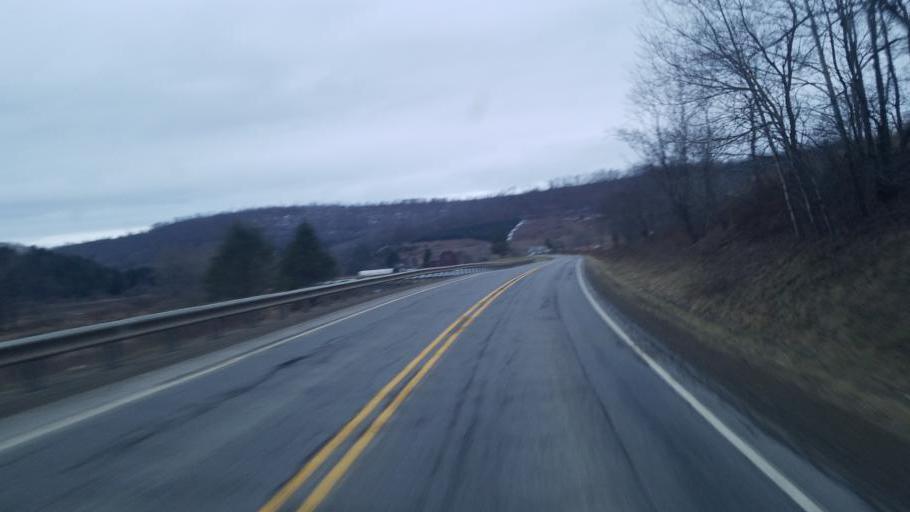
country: US
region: Pennsylvania
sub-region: Potter County
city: Coudersport
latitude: 41.8348
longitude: -77.9338
